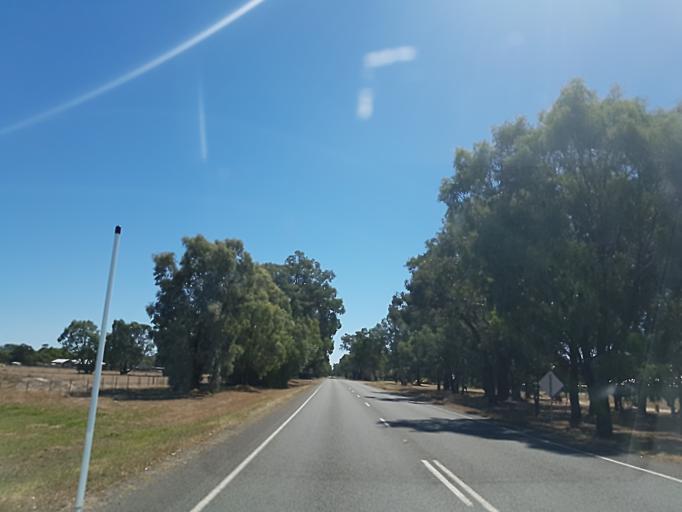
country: AU
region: Victoria
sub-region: Wangaratta
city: Wangaratta
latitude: -36.3942
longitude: 146.4528
